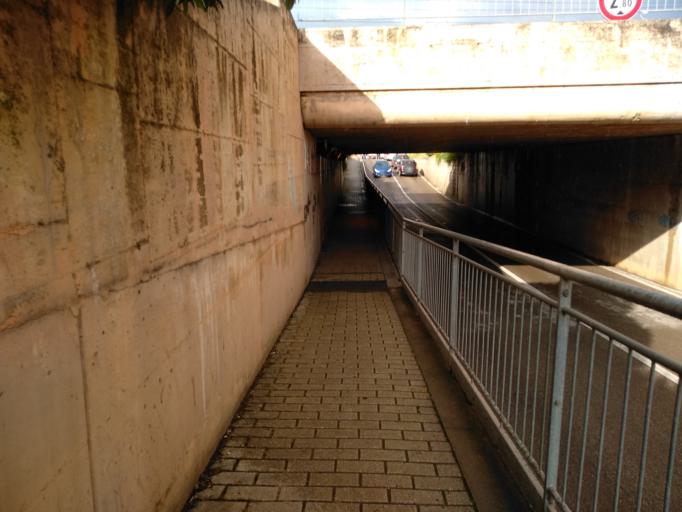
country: IT
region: Tuscany
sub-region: Province of Arezzo
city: San Giovanni Valdarno
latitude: 43.5617
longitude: 11.5303
